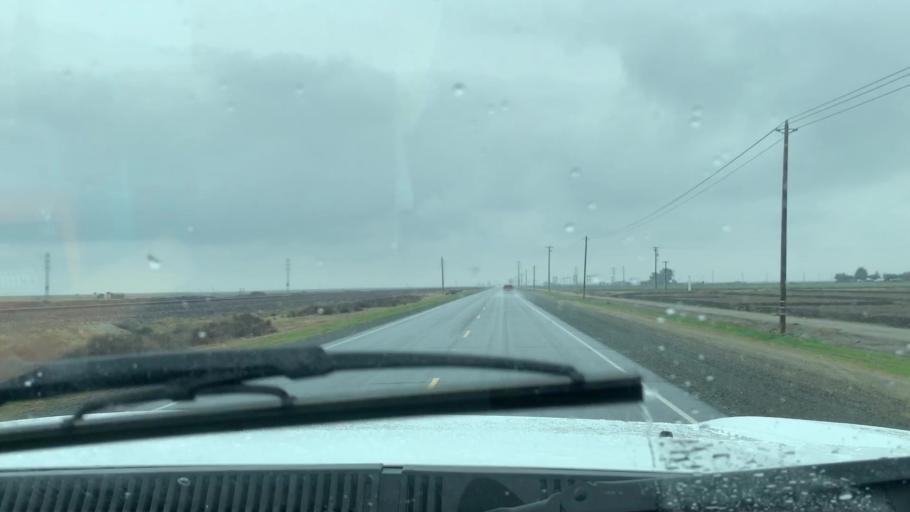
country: US
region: California
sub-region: Tulare County
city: Alpaugh
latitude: 35.9548
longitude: -119.4515
